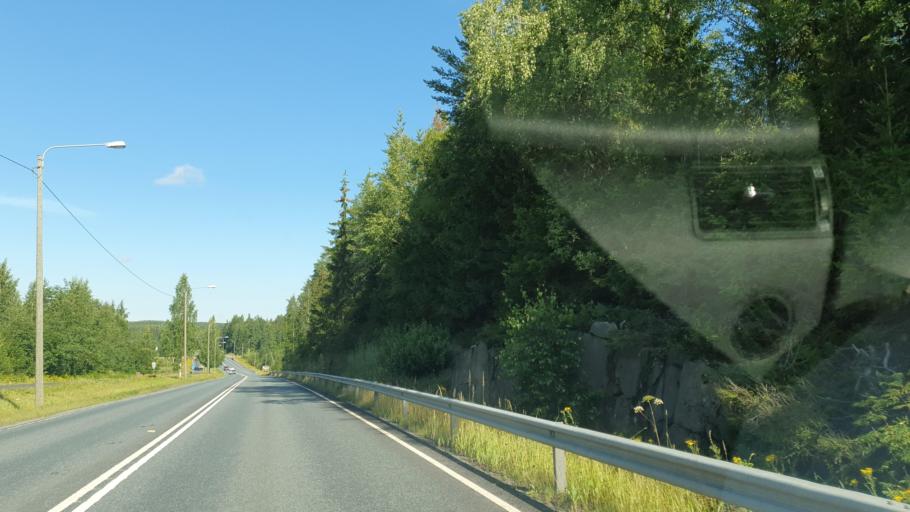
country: FI
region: Northern Savo
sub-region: Kuopio
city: Siilinjaervi
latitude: 63.1339
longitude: 27.6230
